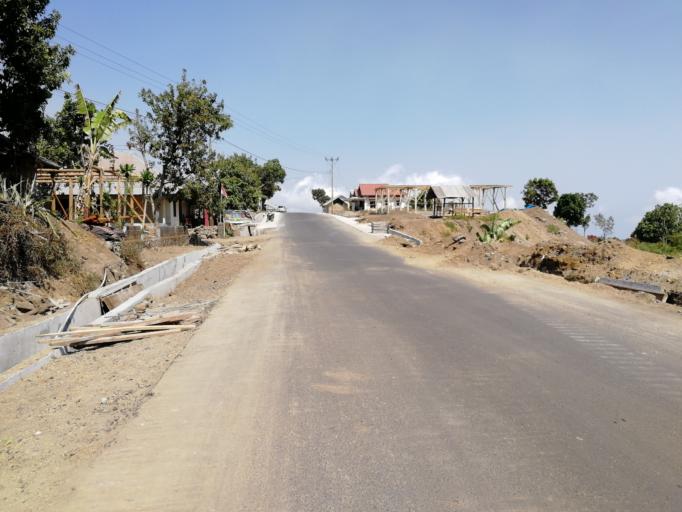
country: ID
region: West Nusa Tenggara
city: Lelongken
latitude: -8.3453
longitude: 116.5077
